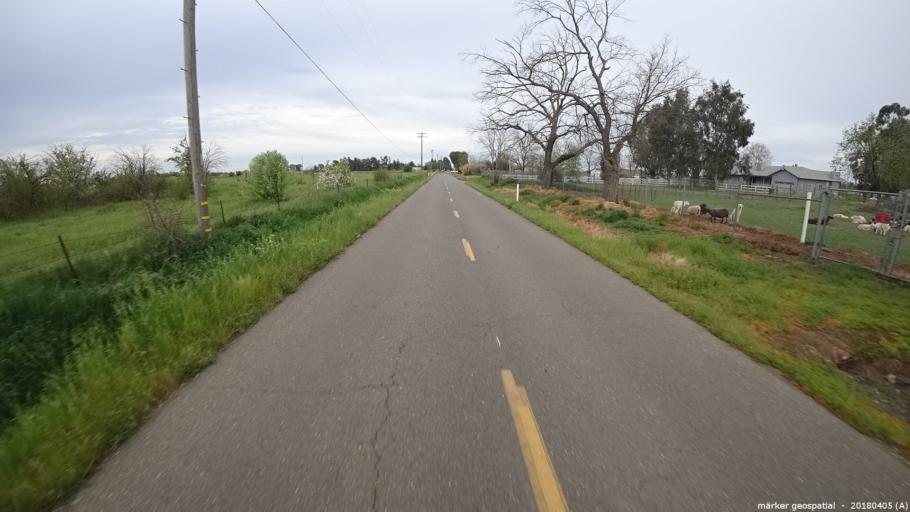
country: US
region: California
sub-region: Sacramento County
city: Herald
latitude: 38.2772
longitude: -121.2424
